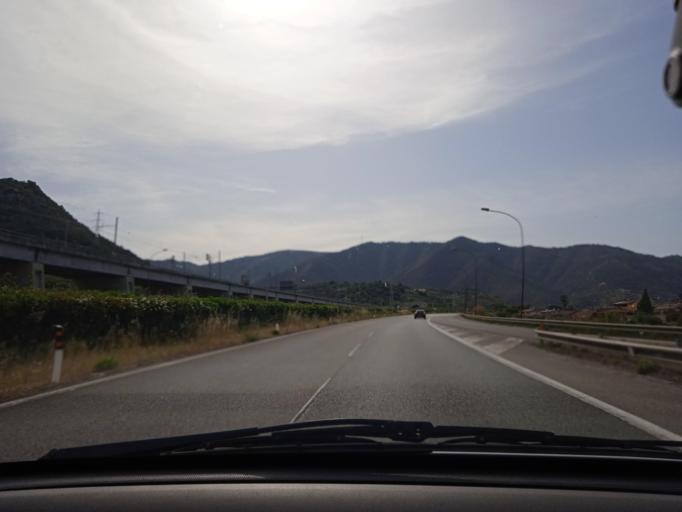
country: IT
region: Sicily
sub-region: Messina
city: Falcone
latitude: 38.1134
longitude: 15.0709
